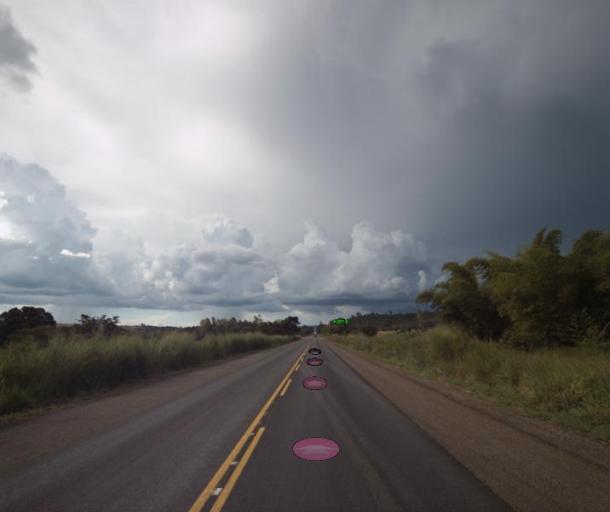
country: BR
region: Goias
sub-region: Ceres
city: Ceres
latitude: -15.2002
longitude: -49.5449
